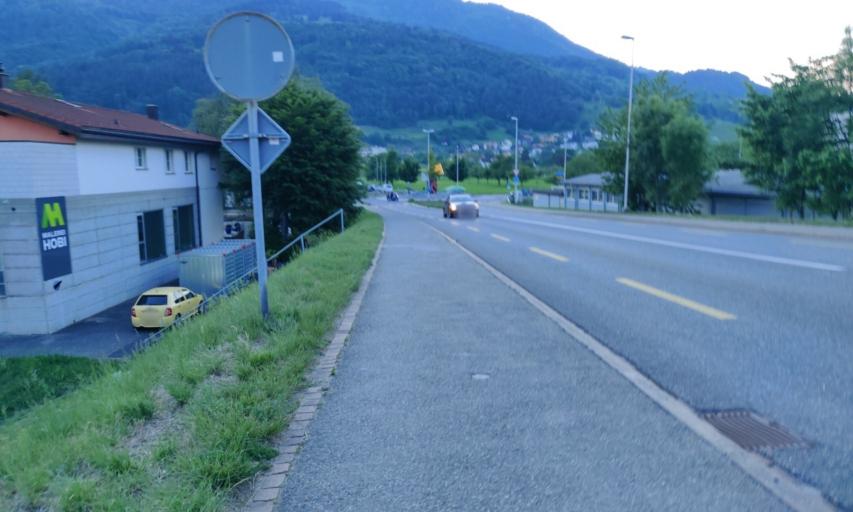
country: LI
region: Balzers
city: Balzers
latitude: 47.0762
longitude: 9.4850
